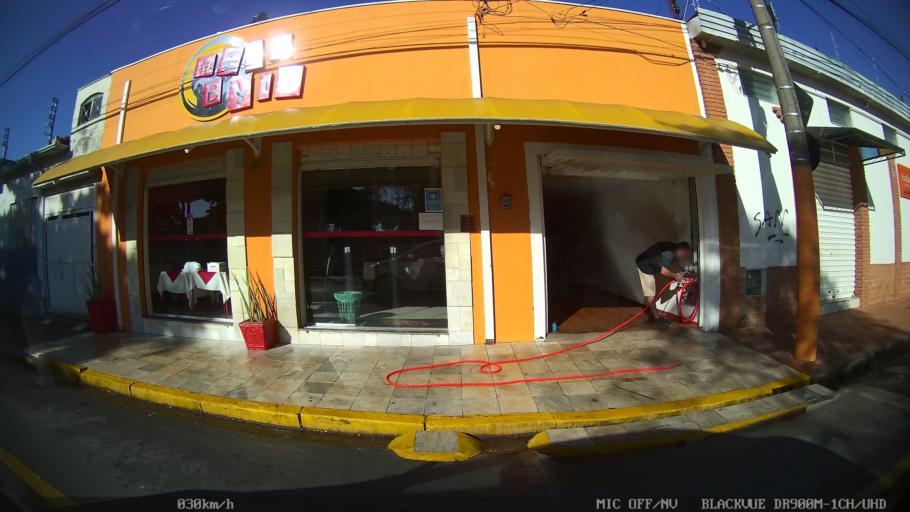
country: BR
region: Sao Paulo
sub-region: Franca
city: Franca
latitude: -20.5307
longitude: -47.4158
